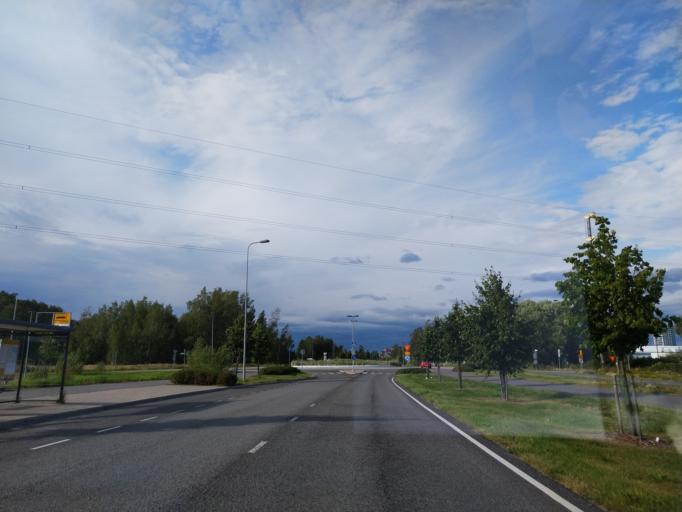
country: FI
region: Varsinais-Suomi
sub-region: Turku
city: Turku
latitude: 60.4208
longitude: 22.2275
